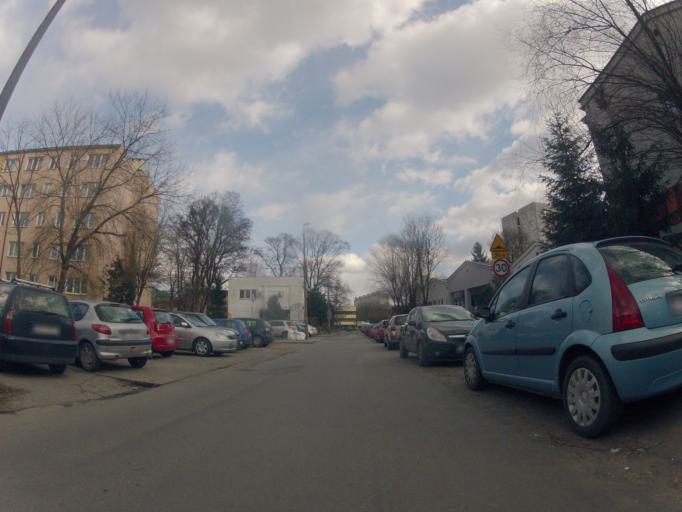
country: PL
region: Lesser Poland Voivodeship
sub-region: Krakow
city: Krakow
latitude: 50.0832
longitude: 19.9733
